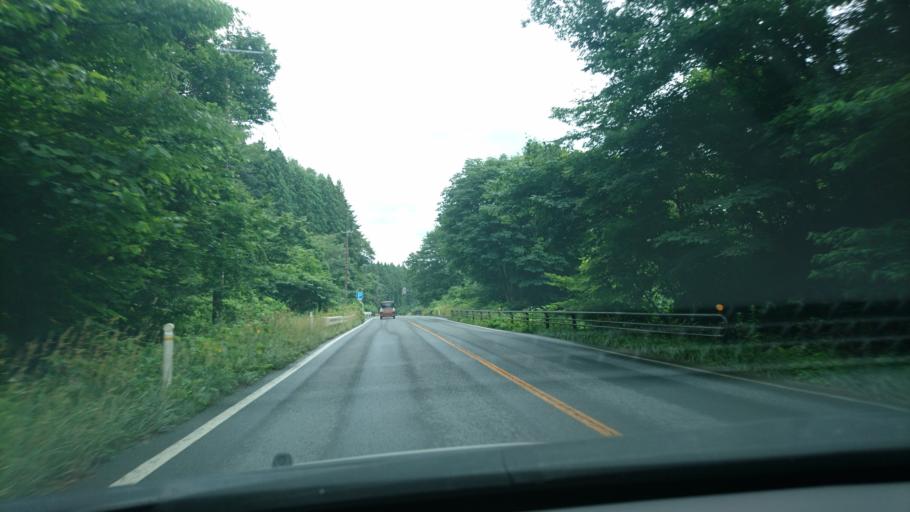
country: JP
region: Iwate
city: Yamada
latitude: 39.4109
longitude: 141.9616
